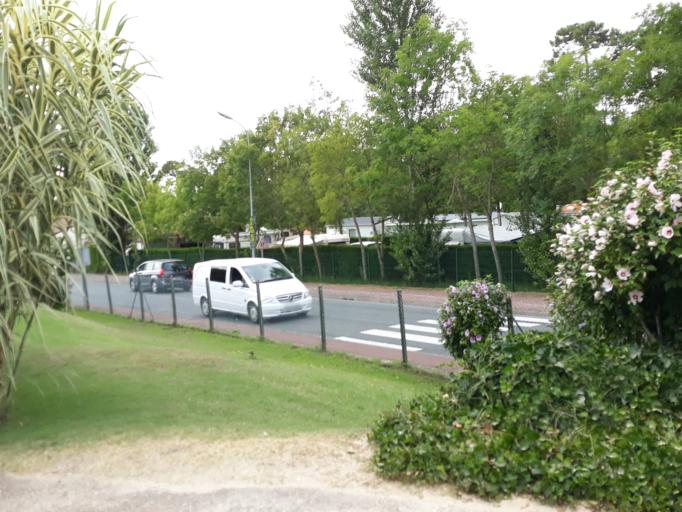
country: FR
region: Poitou-Charentes
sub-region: Departement de la Charente-Maritime
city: Fouras
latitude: 45.9928
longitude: -1.0848
